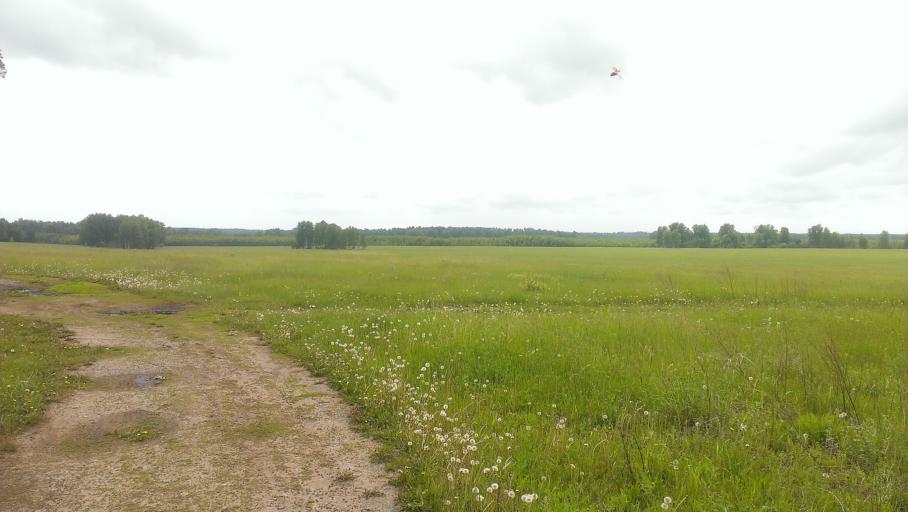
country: RU
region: Altai Krai
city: Bayunovskiye Klyuchi
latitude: 53.3254
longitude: 84.1103
